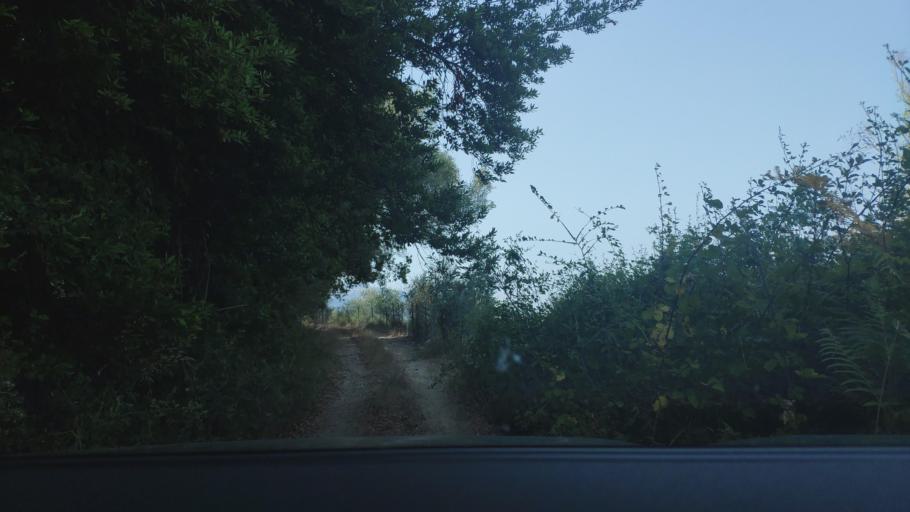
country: GR
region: West Greece
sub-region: Nomos Aitolias kai Akarnanias
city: Fitiai
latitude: 38.7318
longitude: 21.1836
